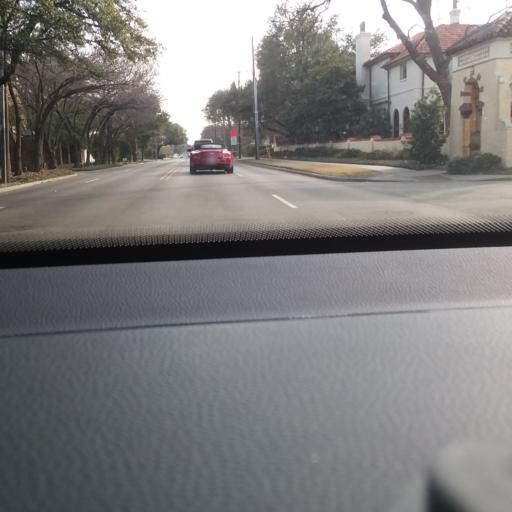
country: US
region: Texas
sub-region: Dallas County
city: University Park
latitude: 32.8424
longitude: -96.8044
